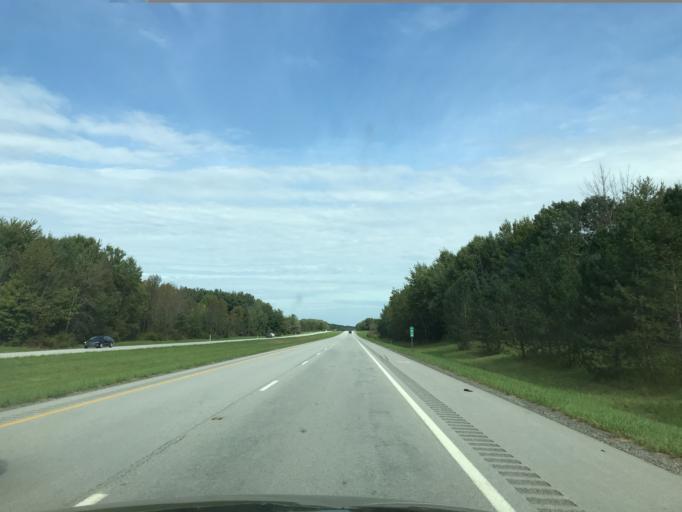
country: US
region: Ohio
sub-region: Ashtabula County
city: Jefferson
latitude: 41.6648
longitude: -80.7134
